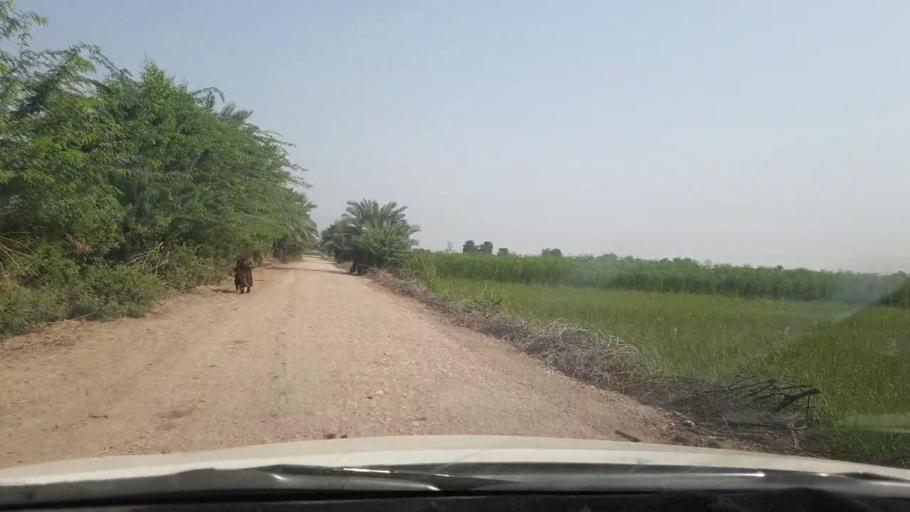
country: PK
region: Sindh
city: Rohri
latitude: 27.6318
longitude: 68.8853
